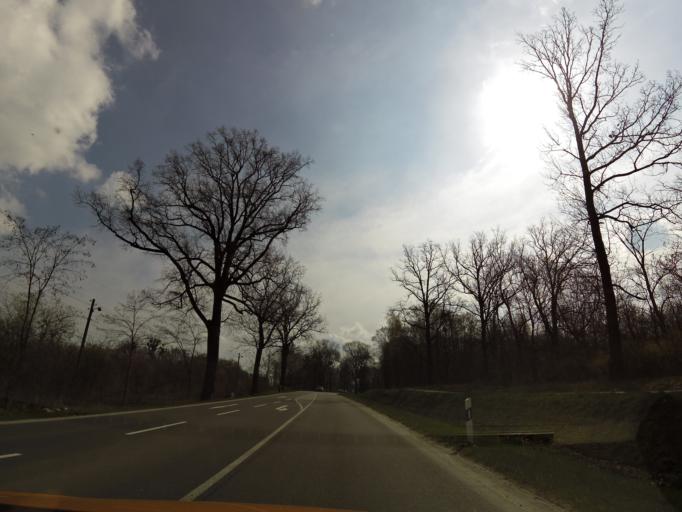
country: DE
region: Brandenburg
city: Petershagen
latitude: 52.4874
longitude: 13.8176
